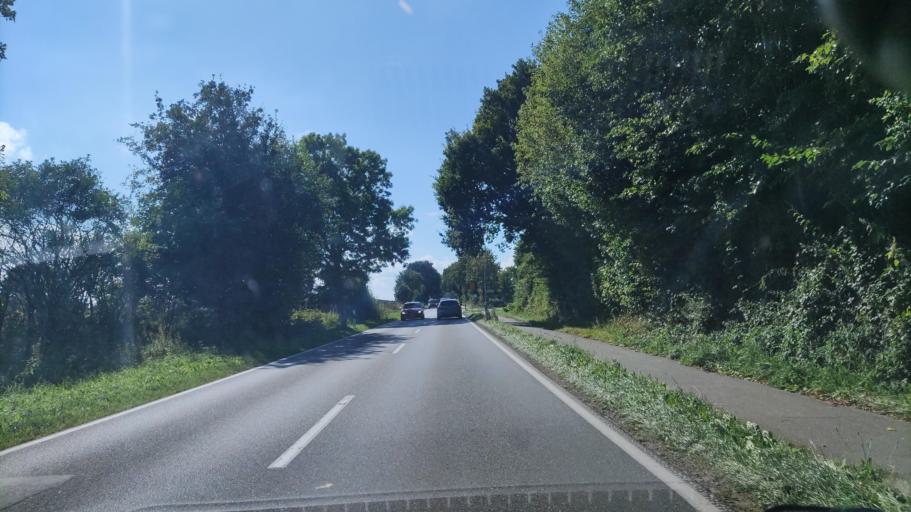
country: DE
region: Schleswig-Holstein
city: Osterby
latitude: 54.4489
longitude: 9.7517
